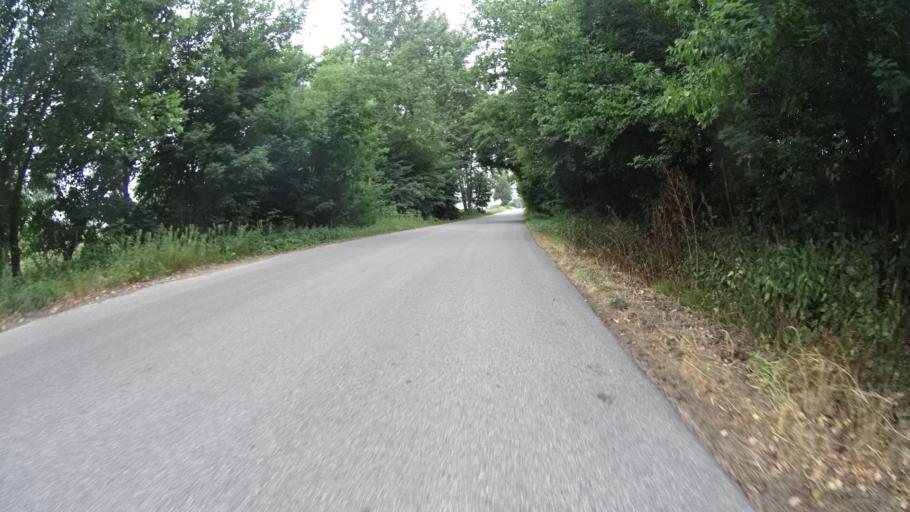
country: PL
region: Masovian Voivodeship
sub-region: Powiat grojecki
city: Goszczyn
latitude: 51.6848
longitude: 20.8614
